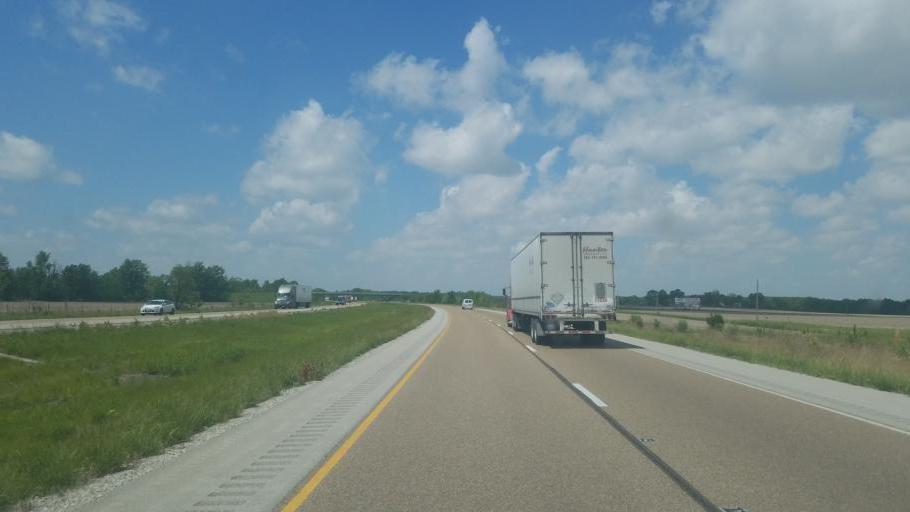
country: US
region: Illinois
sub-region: Cumberland County
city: Greenup
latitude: 39.2744
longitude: -88.1035
